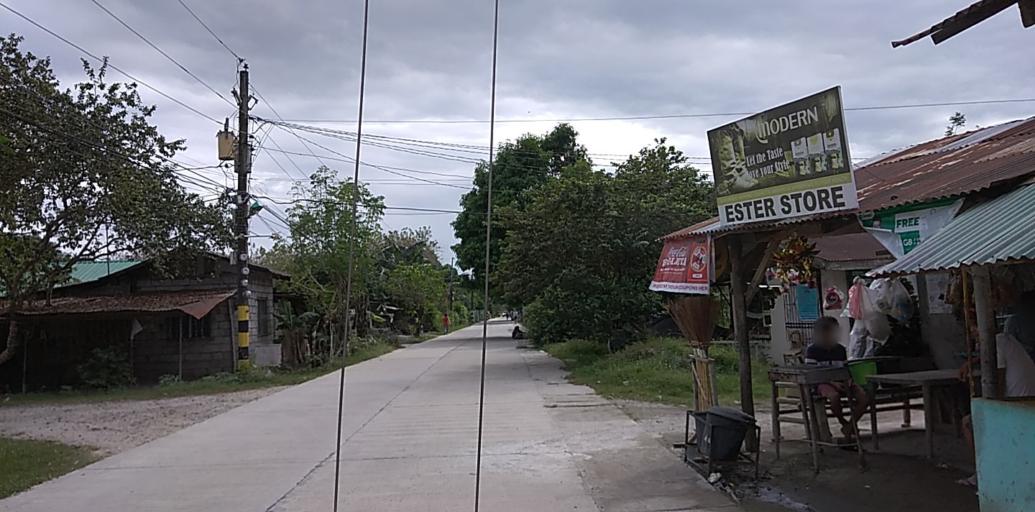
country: PH
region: Central Luzon
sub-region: Province of Pampanga
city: Pulung Santol
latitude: 15.0469
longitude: 120.5558
